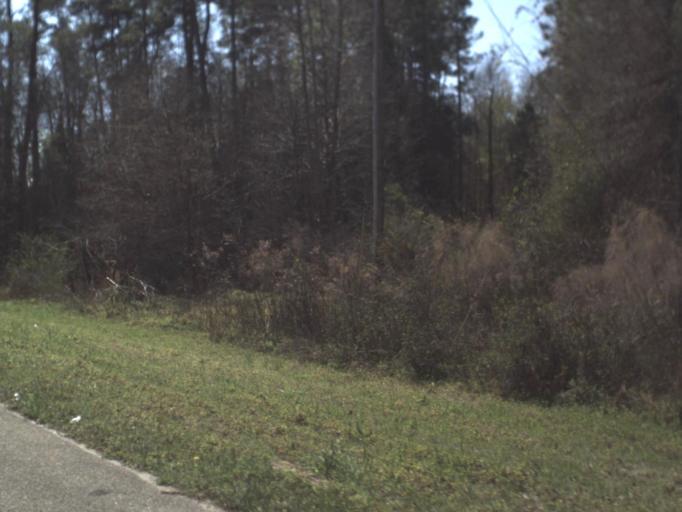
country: US
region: Florida
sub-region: Calhoun County
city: Blountstown
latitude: 30.4803
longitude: -85.0460
